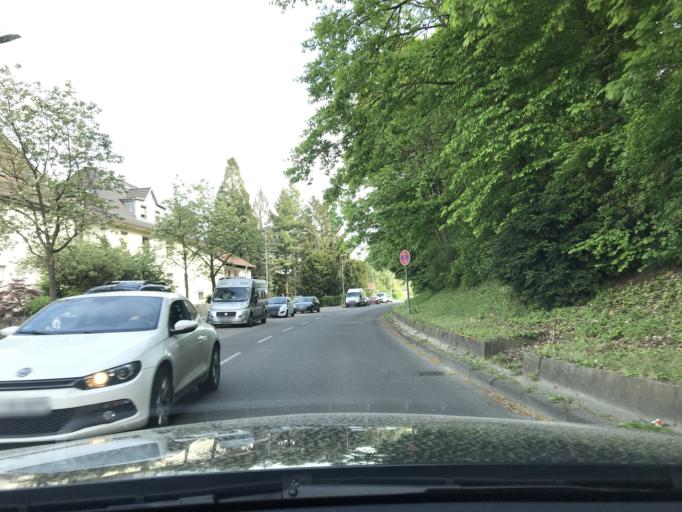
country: DE
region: Baden-Wuerttemberg
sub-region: Regierungsbezirk Stuttgart
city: Waiblingen
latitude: 48.8262
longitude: 9.3249
